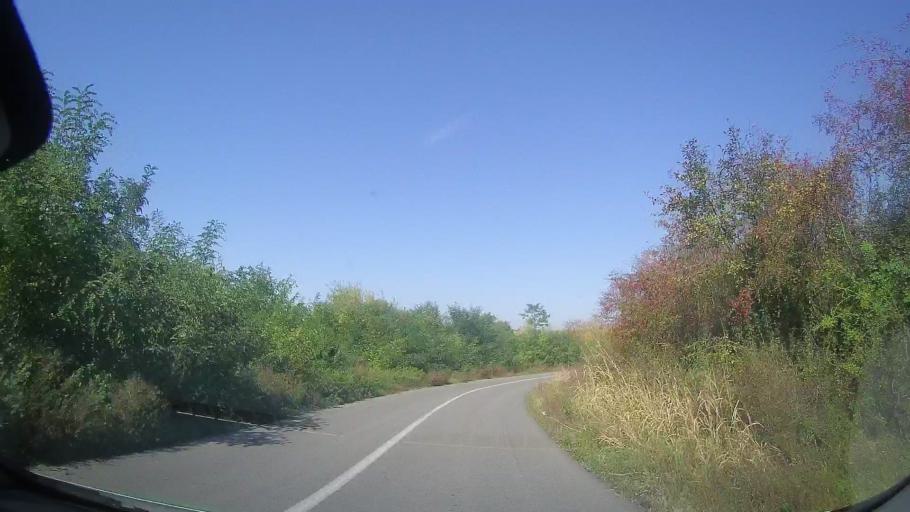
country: RO
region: Timis
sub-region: Comuna Balint
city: Balint
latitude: 45.8378
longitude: 21.8554
